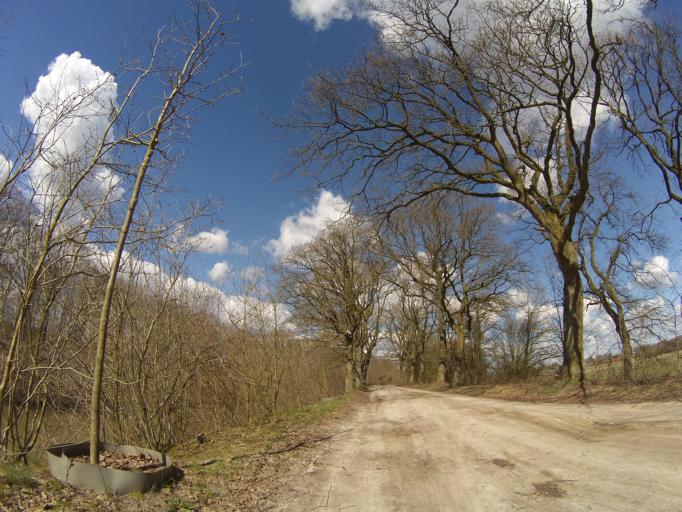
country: NL
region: Drenthe
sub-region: Gemeente Emmen
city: Emmen
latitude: 52.7779
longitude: 6.8741
